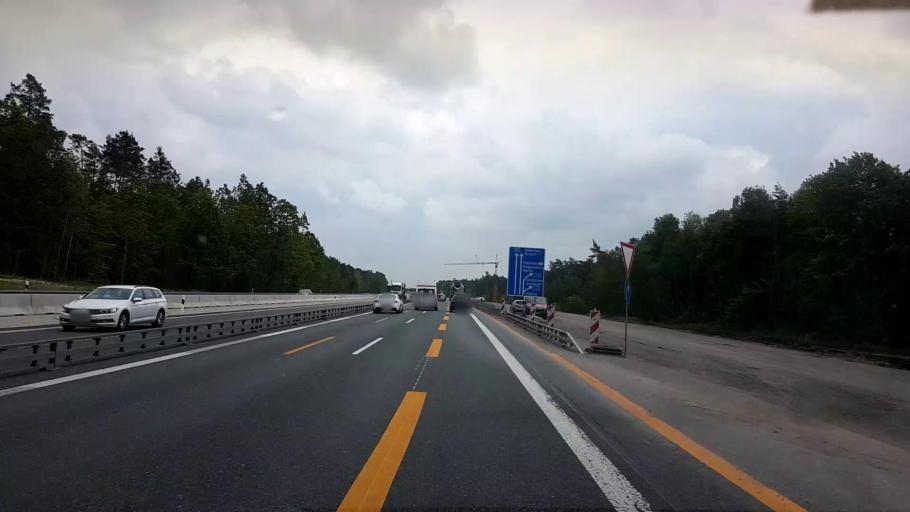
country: DE
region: Bavaria
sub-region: Regierungsbezirk Mittelfranken
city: Wendelstein
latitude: 49.3884
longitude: 11.1213
